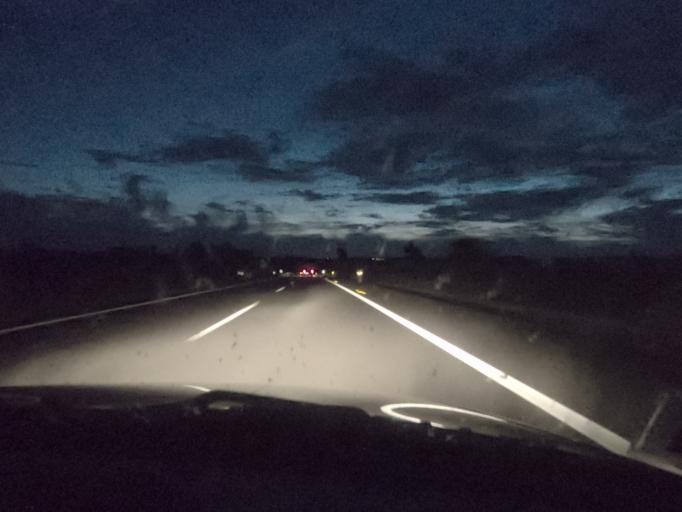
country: ES
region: Extremadura
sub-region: Provincia de Caceres
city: Morcillo
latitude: 39.9815
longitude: -6.4044
